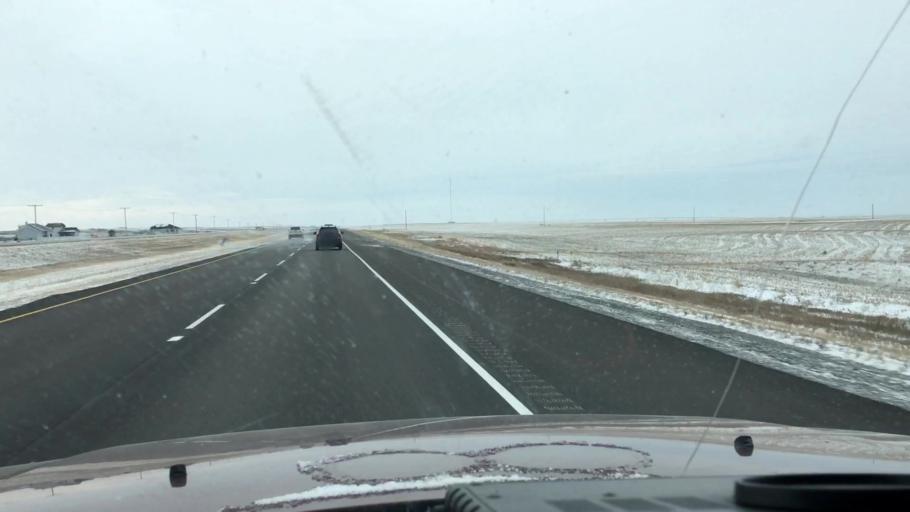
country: CA
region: Saskatchewan
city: Saskatoon
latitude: 51.7547
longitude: -106.4764
